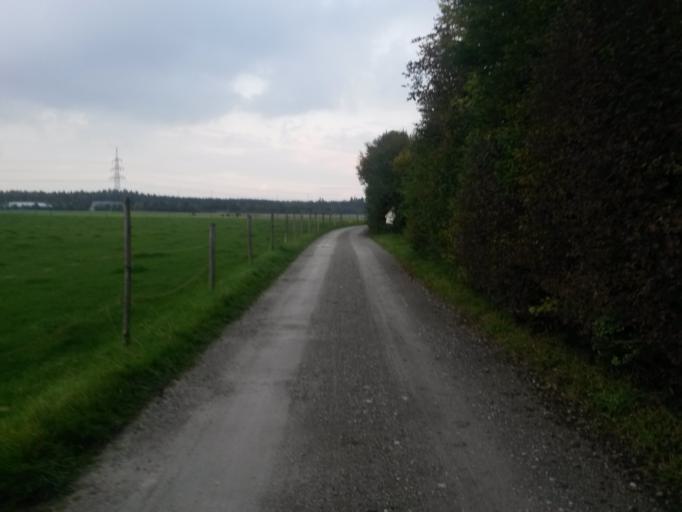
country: DE
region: Bavaria
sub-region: Upper Bavaria
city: Grasbrunn
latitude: 48.0828
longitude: 11.7492
